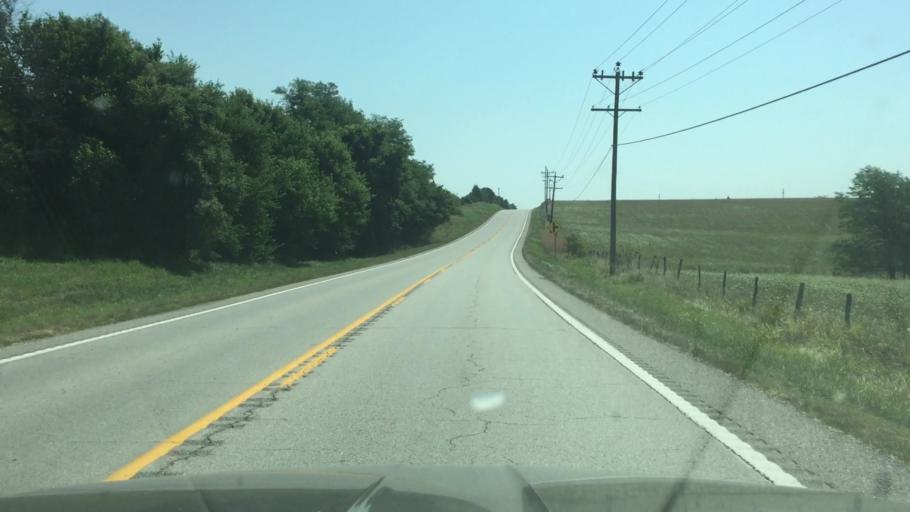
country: US
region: Missouri
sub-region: Moniteau County
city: Tipton
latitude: 38.6710
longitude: -92.8678
